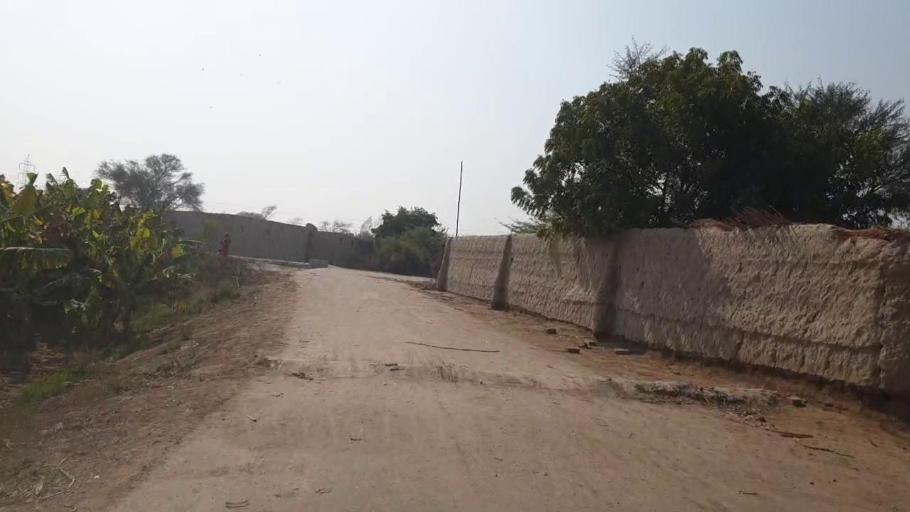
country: PK
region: Sindh
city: Bhit Shah
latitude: 25.7756
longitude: 68.4797
